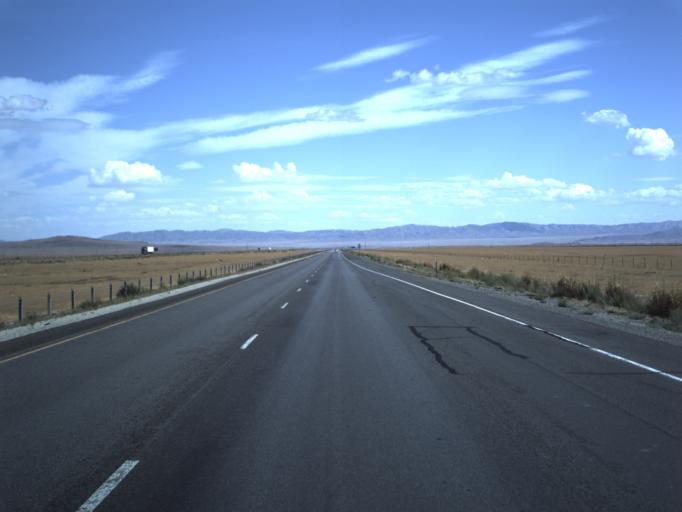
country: US
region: Utah
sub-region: Tooele County
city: Wendover
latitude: 40.7263
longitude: -113.2499
